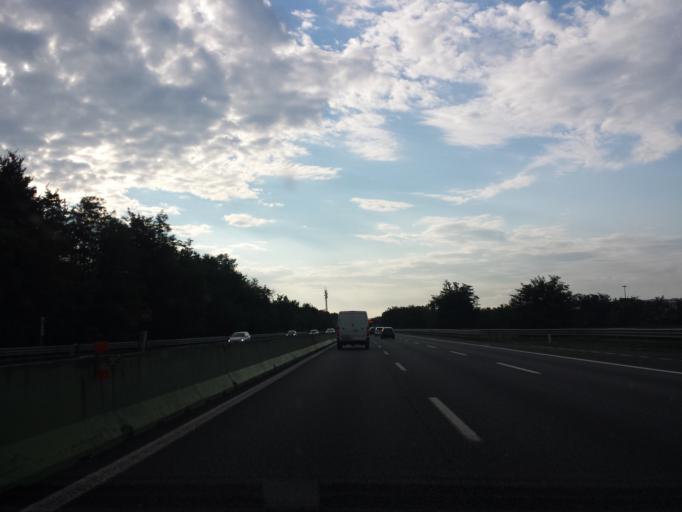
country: IT
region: Lombardy
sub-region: Citta metropolitana di Milano
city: Cantalupo
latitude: 45.5860
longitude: 8.9857
